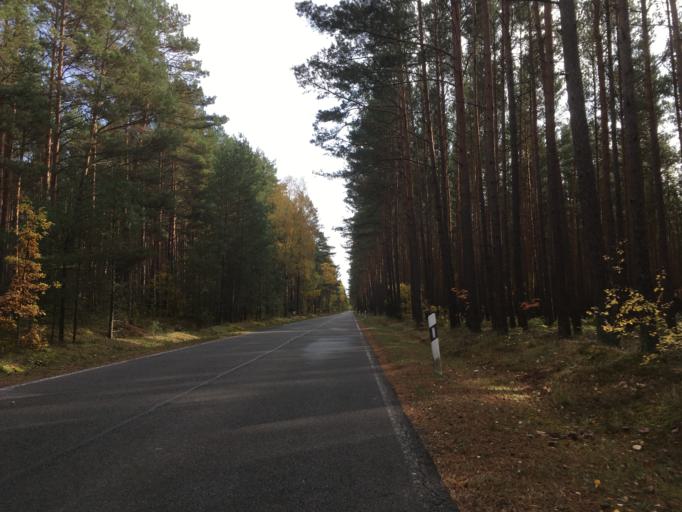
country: DE
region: Brandenburg
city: Templin
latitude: 53.0349
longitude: 13.4704
